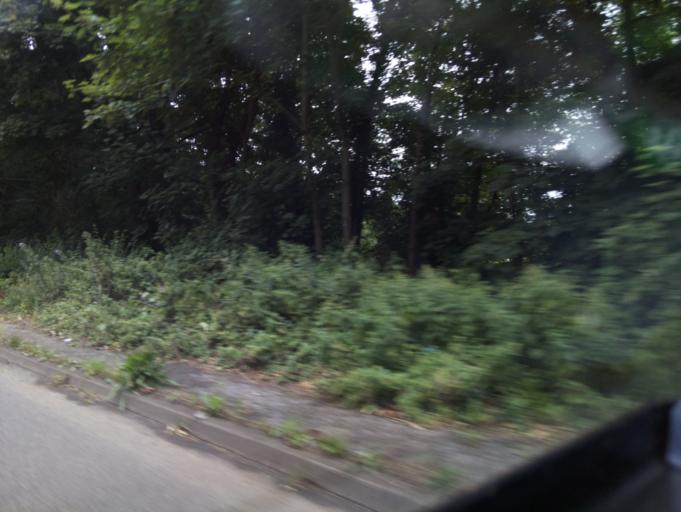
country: GB
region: England
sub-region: Gloucestershire
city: Tewkesbury
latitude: 52.0257
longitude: -2.1633
